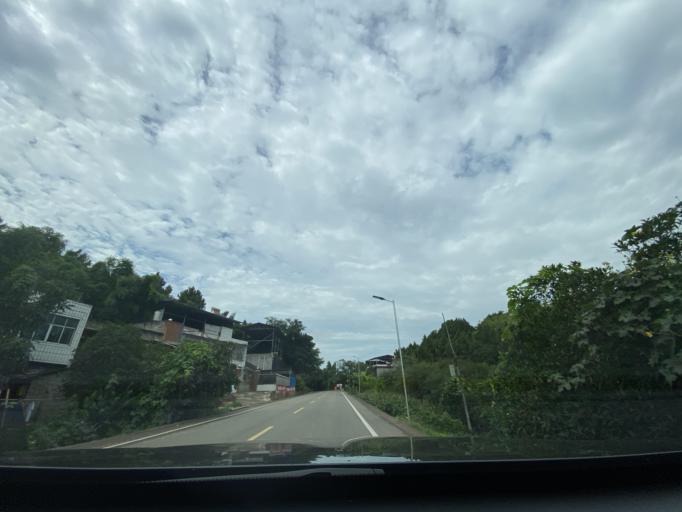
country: CN
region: Sichuan
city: Jiancheng
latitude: 30.4810
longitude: 104.6331
